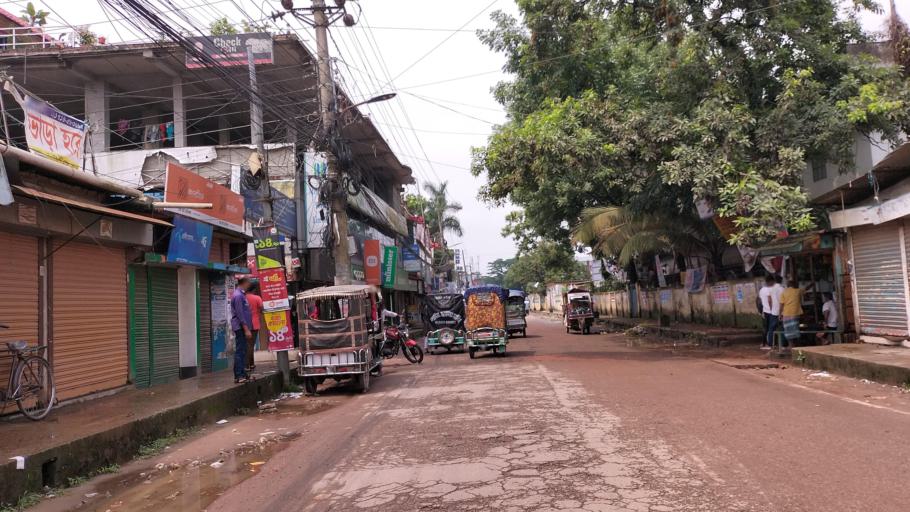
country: BD
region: Dhaka
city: Netrakona
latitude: 24.8764
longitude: 90.7301
